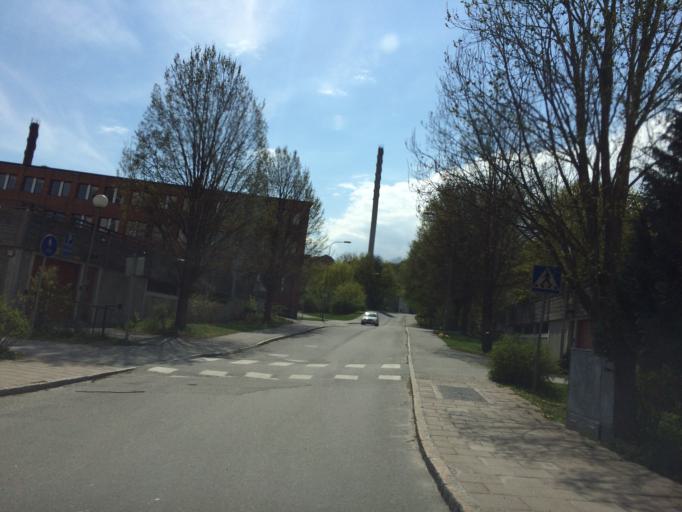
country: SE
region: Stockholm
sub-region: Stockholms Kommun
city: Bromma
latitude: 59.3070
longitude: 17.9812
